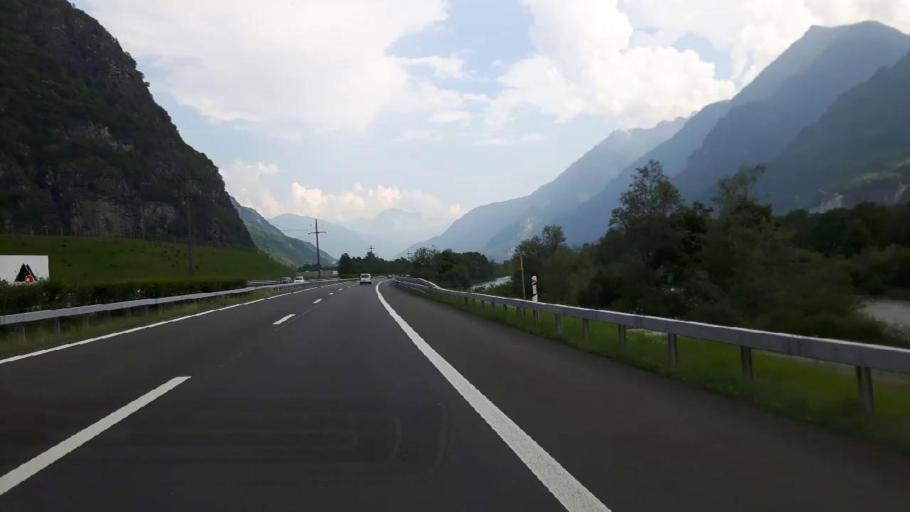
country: CH
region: Ticino
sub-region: Riviera District
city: Lodrino
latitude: 46.3268
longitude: 8.9791
